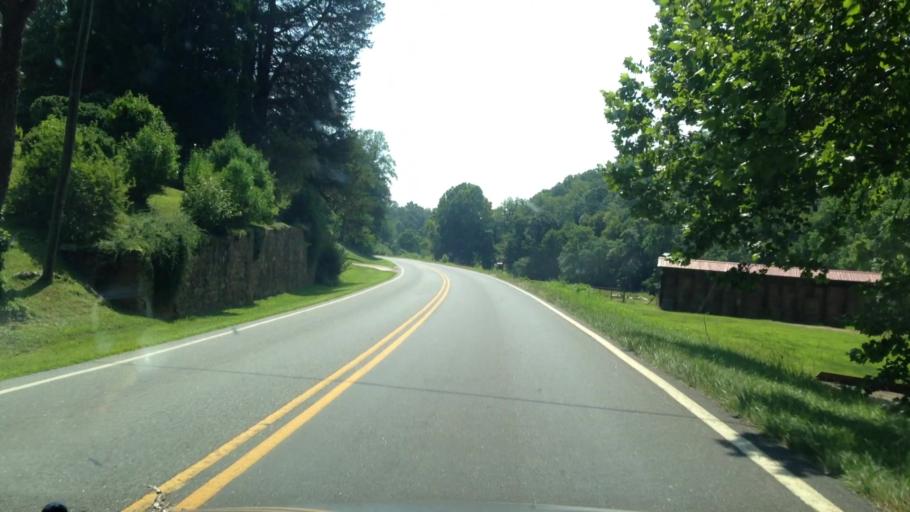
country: US
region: Virginia
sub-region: Patrick County
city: Stuart
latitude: 36.5876
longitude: -80.4061
